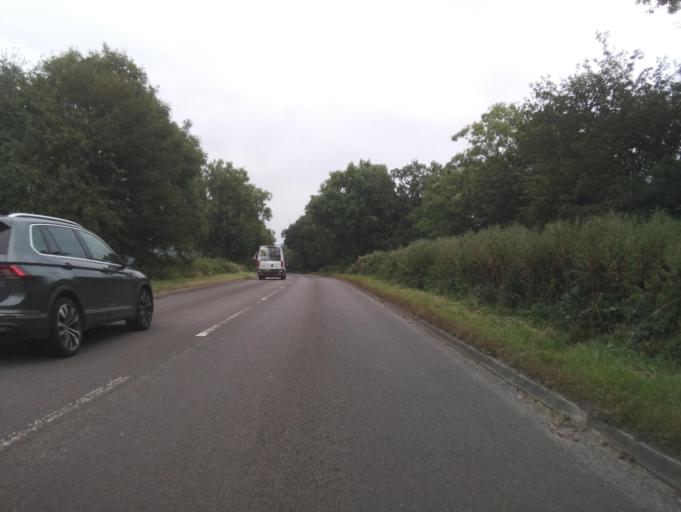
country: GB
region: England
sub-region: Staffordshire
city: Mayfield
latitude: 53.0173
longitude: -1.7819
